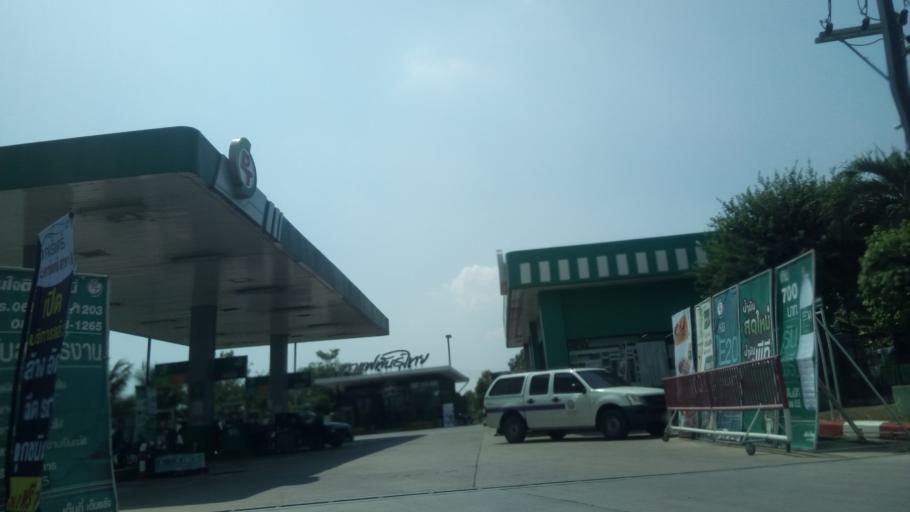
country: TH
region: Nakhon Pathom
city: Salaya
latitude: 13.7586
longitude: 100.2833
